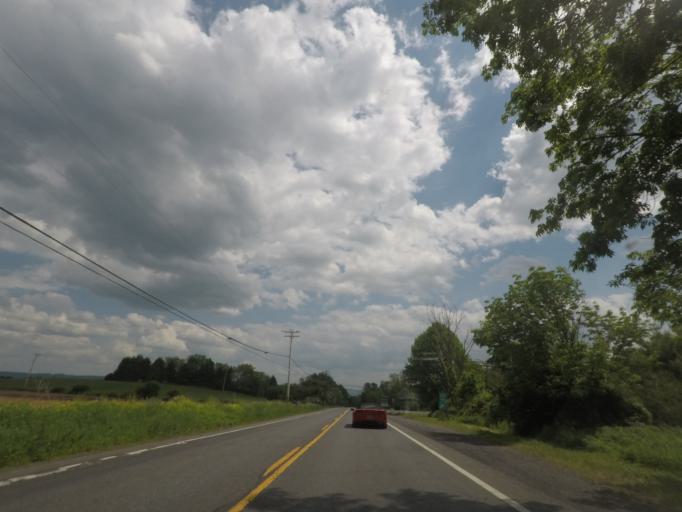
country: US
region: New York
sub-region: Dutchess County
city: Dover Plains
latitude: 41.8891
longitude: -73.5301
